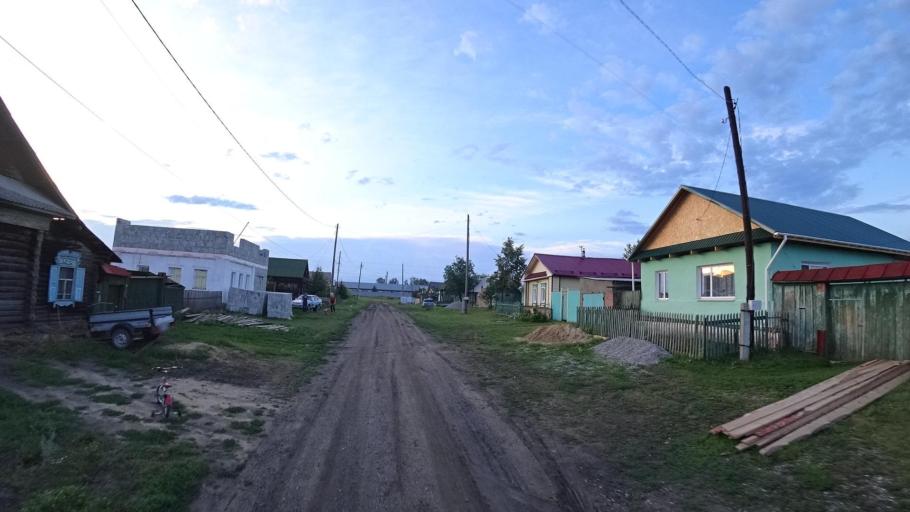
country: RU
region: Sverdlovsk
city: Kamyshlov
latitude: 56.8620
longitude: 62.7132
